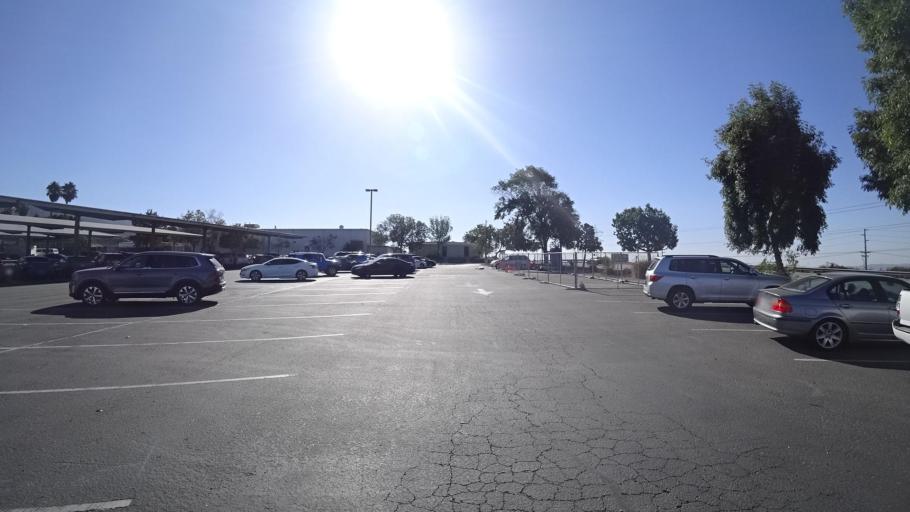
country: MX
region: Baja California
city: Tijuana
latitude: 32.5890
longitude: -116.9215
